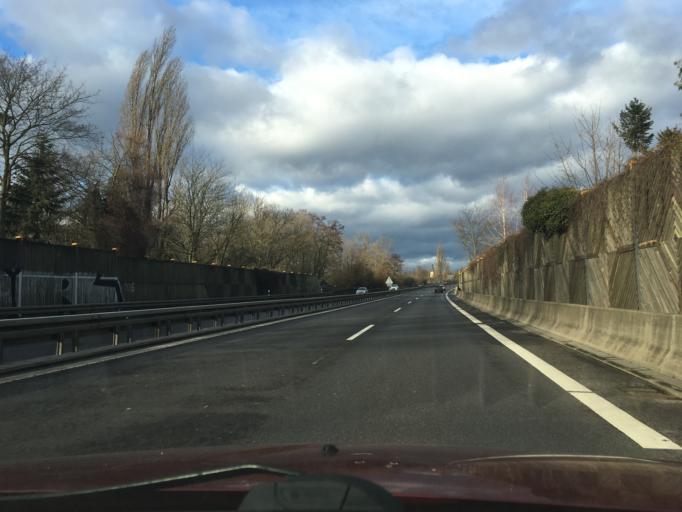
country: DE
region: Berlin
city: Bohnsdorf
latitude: 52.3951
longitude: 13.5628
